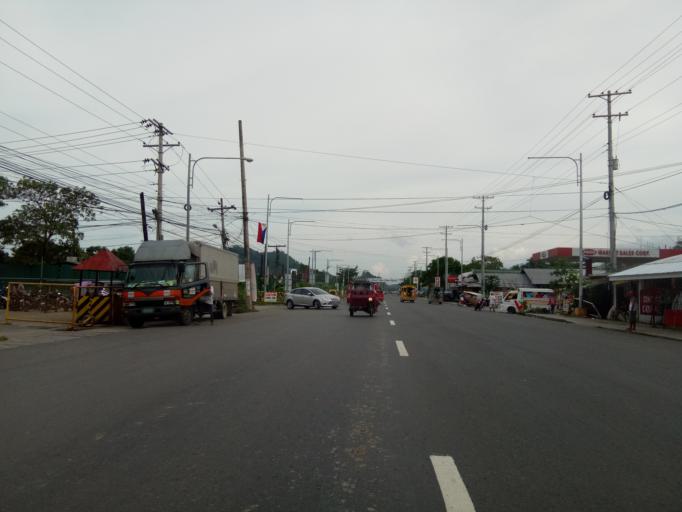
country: PH
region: Caraga
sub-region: Province of Surigao del Norte
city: Rizal
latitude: 9.7640
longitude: 125.4831
